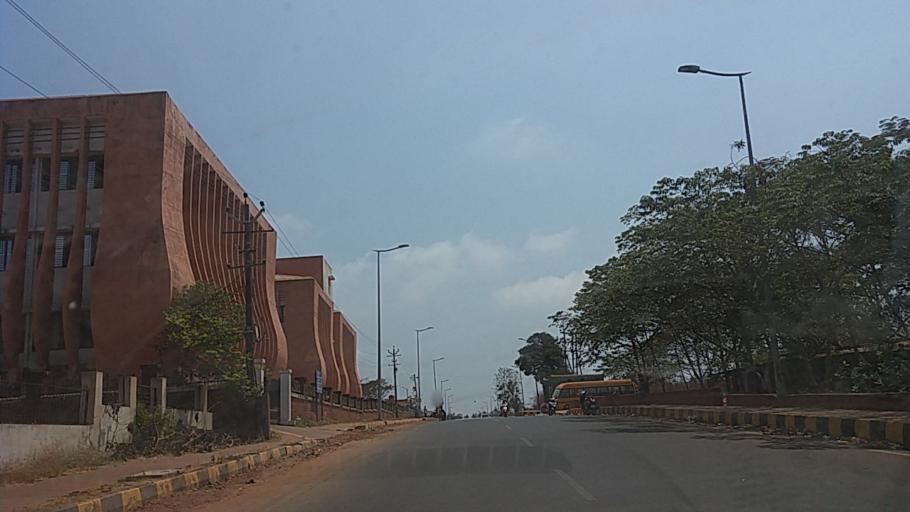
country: IN
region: Goa
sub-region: North Goa
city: Serula
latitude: 15.5242
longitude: 73.8286
